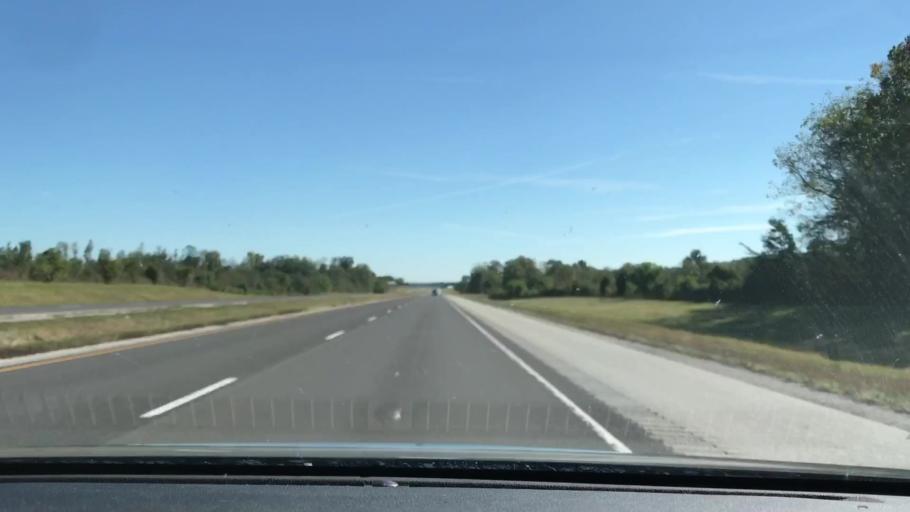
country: US
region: Kentucky
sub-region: Todd County
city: Elkton
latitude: 36.8032
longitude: -87.0813
